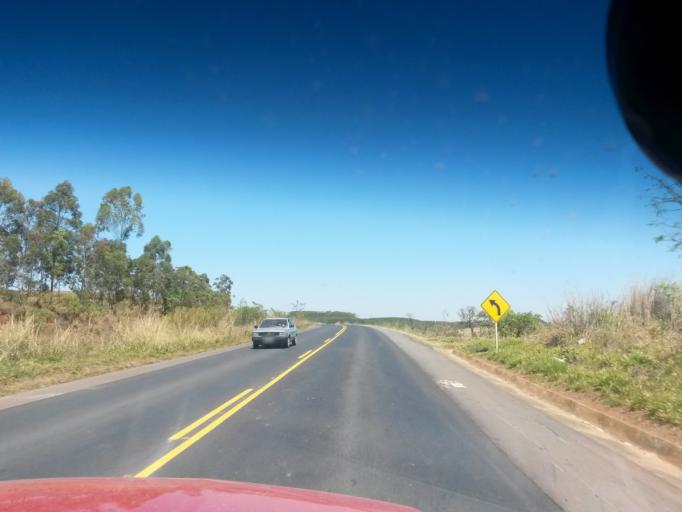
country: BR
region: Minas Gerais
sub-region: Bambui
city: Bambui
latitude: -19.9884
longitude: -45.9607
